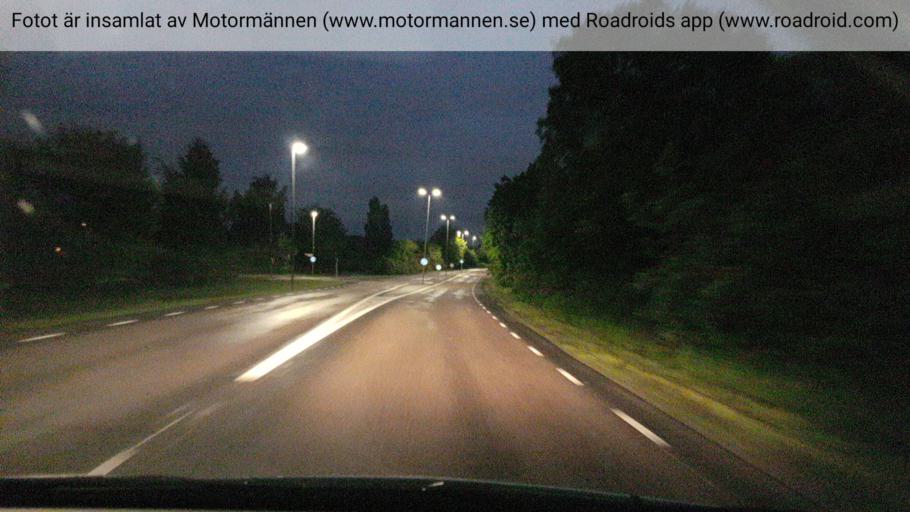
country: SE
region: Vaestmanland
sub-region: Vasteras
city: Vasteras
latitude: 59.6458
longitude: 16.5287
